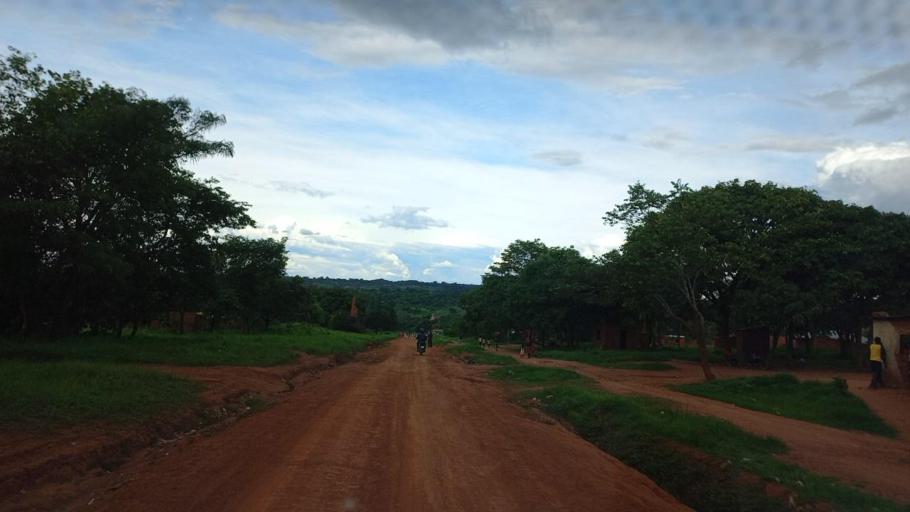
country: ZM
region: North-Western
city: Mwinilunga
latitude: -11.7571
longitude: 24.4316
